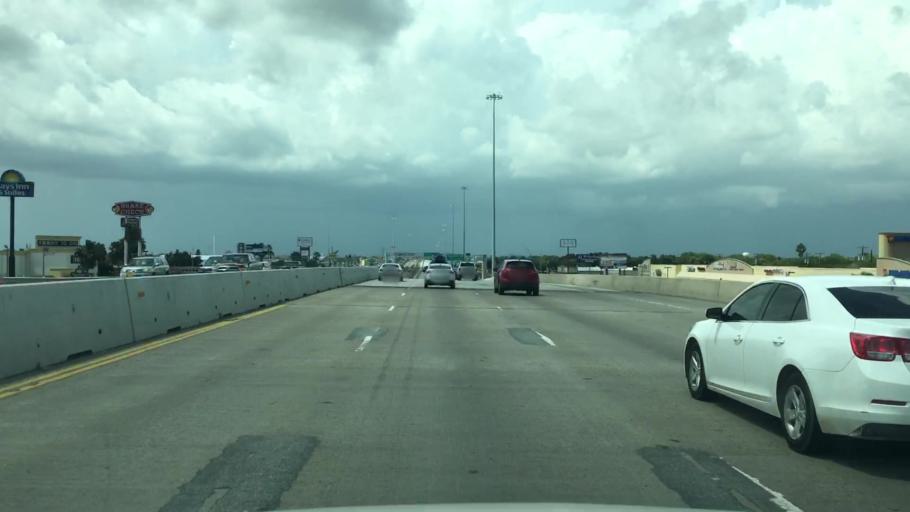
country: US
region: Texas
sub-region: Nueces County
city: Corpus Christi
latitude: 27.7217
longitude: -97.3985
